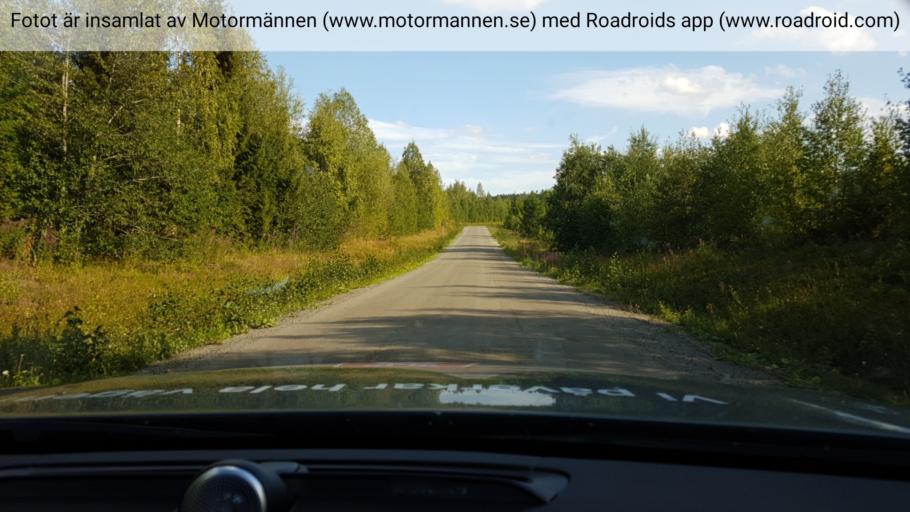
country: SE
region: Vaesternorrland
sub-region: Solleftea Kommun
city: As
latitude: 63.7740
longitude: 16.3141
